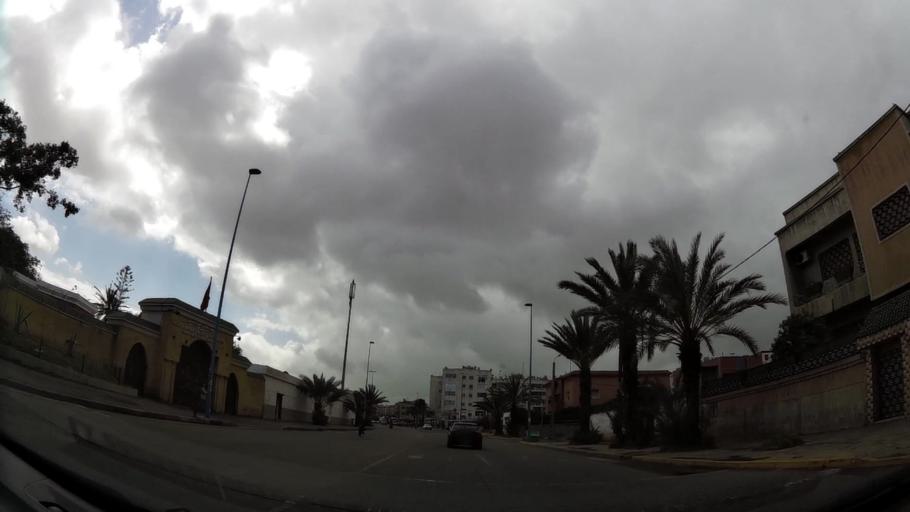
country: MA
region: Grand Casablanca
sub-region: Casablanca
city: Casablanca
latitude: 33.5410
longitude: -7.6006
